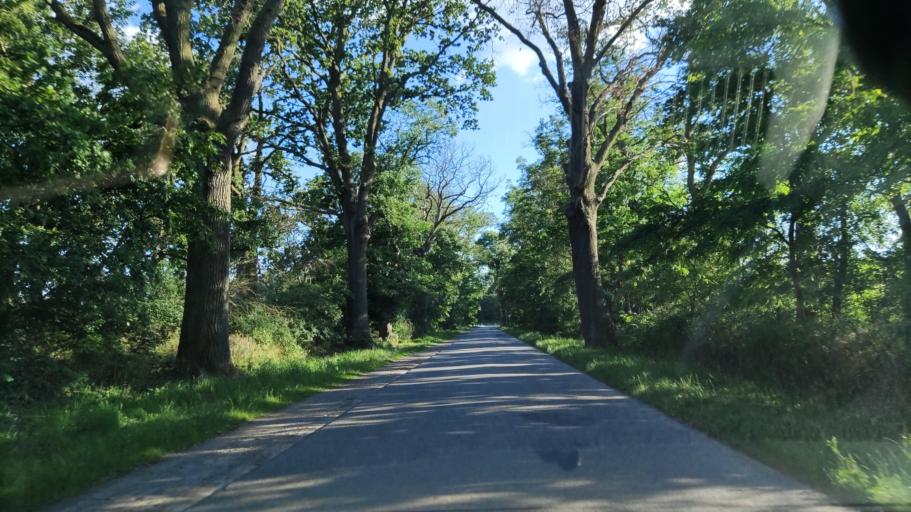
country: DE
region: Lower Saxony
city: Gartow
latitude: 53.0272
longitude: 11.4872
